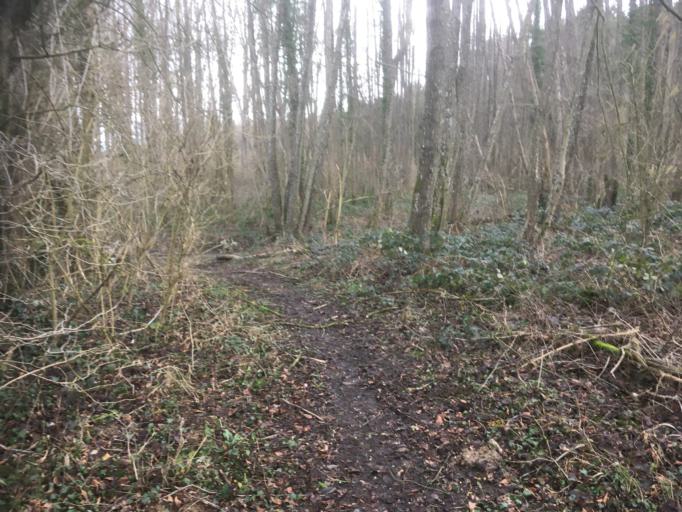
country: BE
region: Wallonia
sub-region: Province du Luxembourg
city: Durbuy
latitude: 50.3067
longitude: 5.4923
